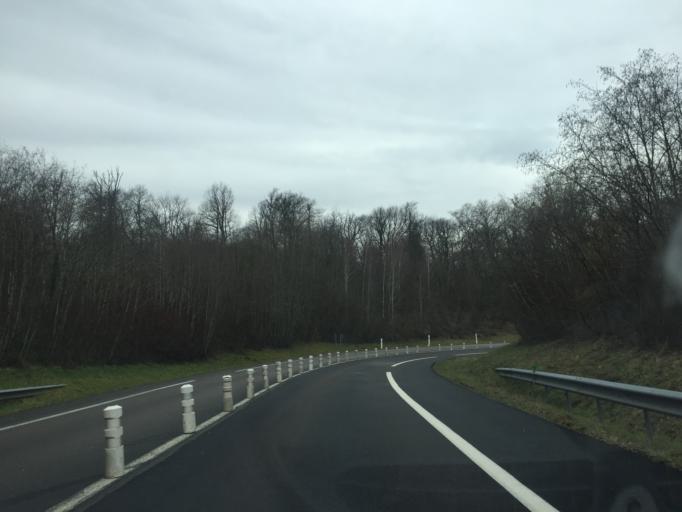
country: FR
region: Franche-Comte
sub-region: Departement du Jura
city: Mont-sous-Vaudrey
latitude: 46.8528
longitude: 5.5705
